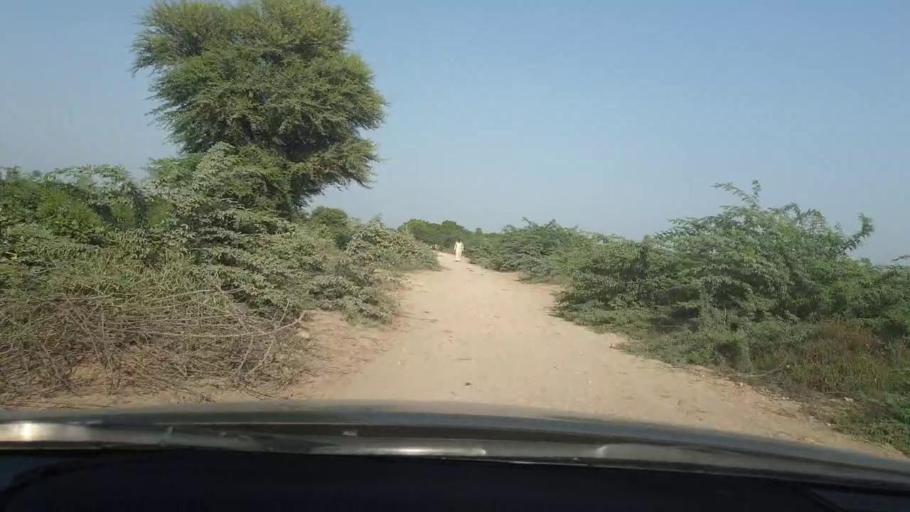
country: PK
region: Sindh
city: Naukot
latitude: 24.7774
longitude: 69.2626
